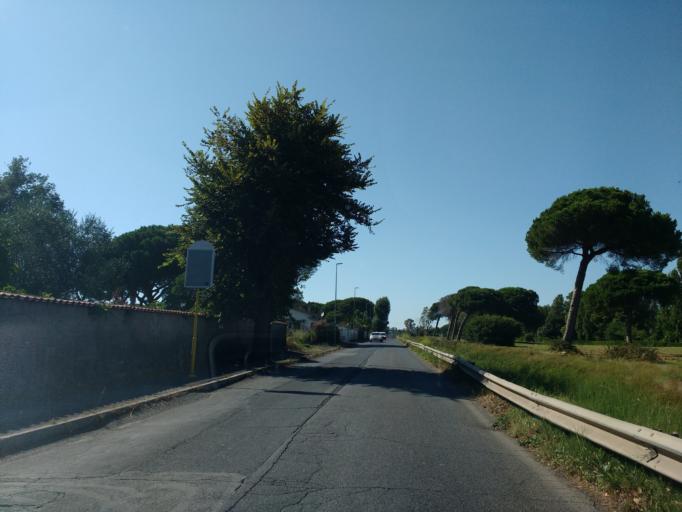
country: IT
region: Latium
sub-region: Citta metropolitana di Roma Capitale
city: Acilia-Castel Fusano-Ostia Antica
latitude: 41.7406
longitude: 12.3410
